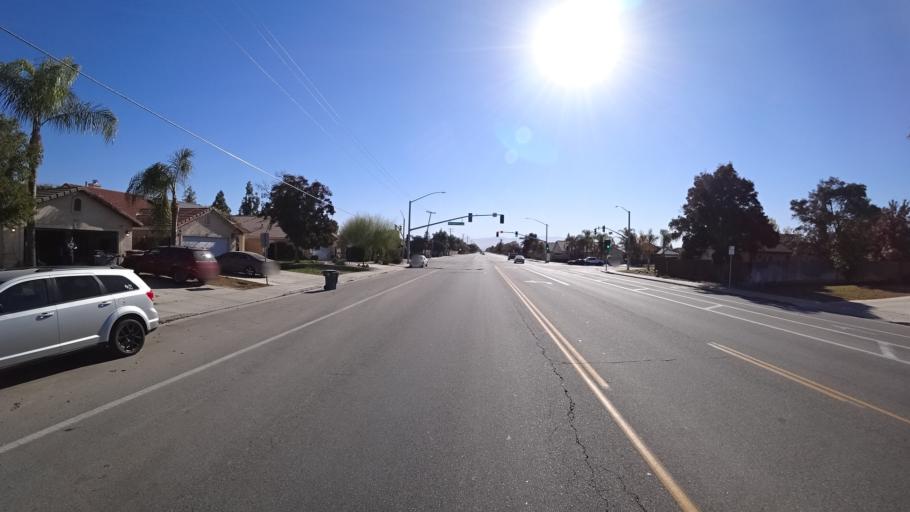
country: US
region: California
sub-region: Kern County
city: Greenfield
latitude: 35.2893
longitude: -119.0478
